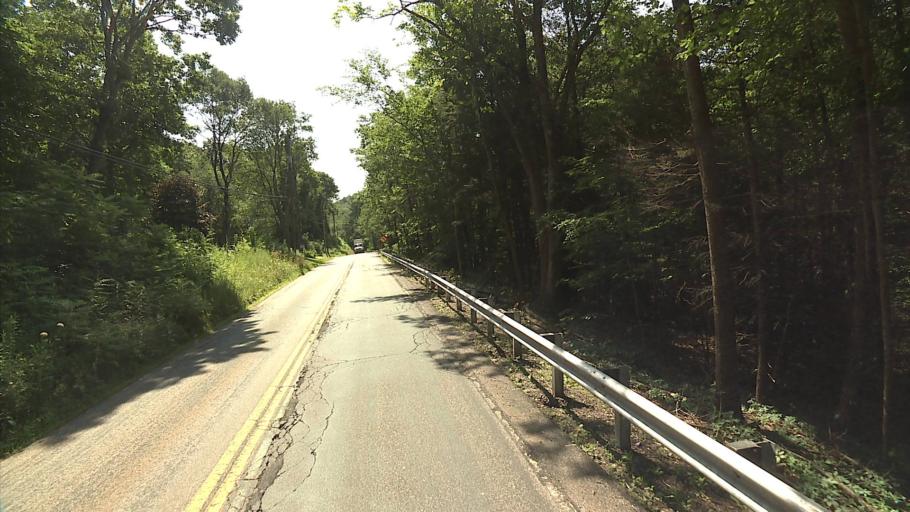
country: US
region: Connecticut
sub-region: Litchfield County
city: Winchester Center
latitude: 41.9183
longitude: -73.1958
